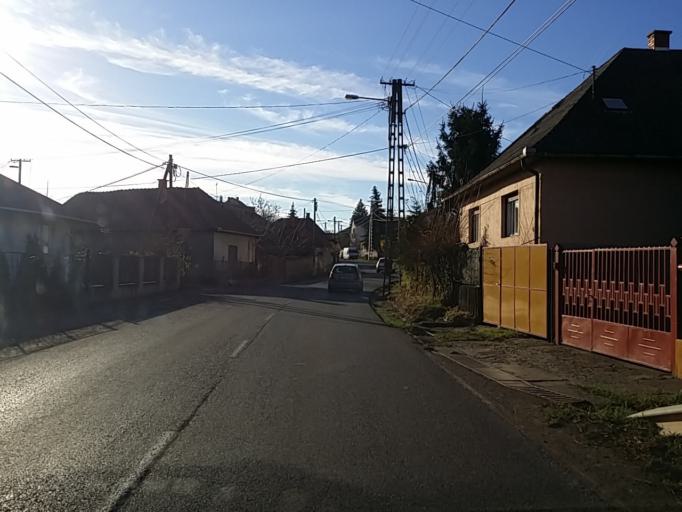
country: HU
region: Heves
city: Abasar
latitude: 47.7977
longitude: 20.0006
